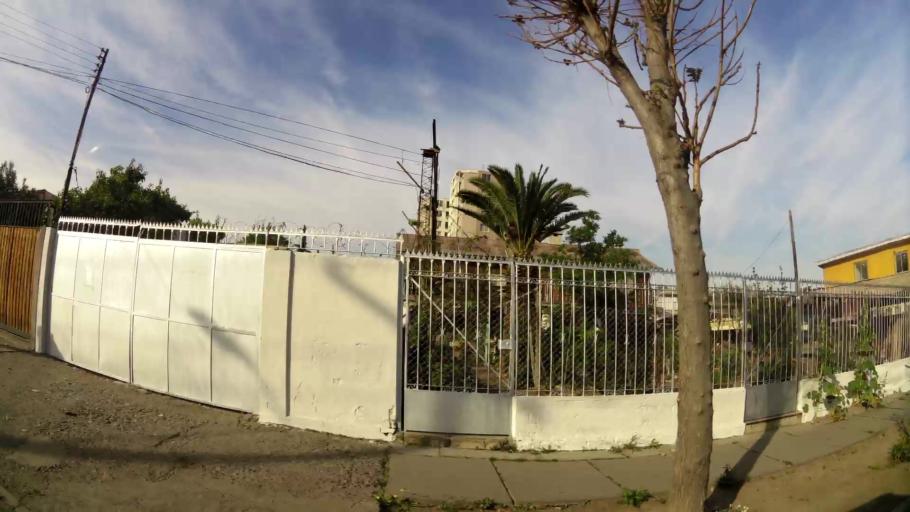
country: CL
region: Santiago Metropolitan
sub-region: Provincia de Santiago
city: Santiago
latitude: -33.5142
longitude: -70.6654
